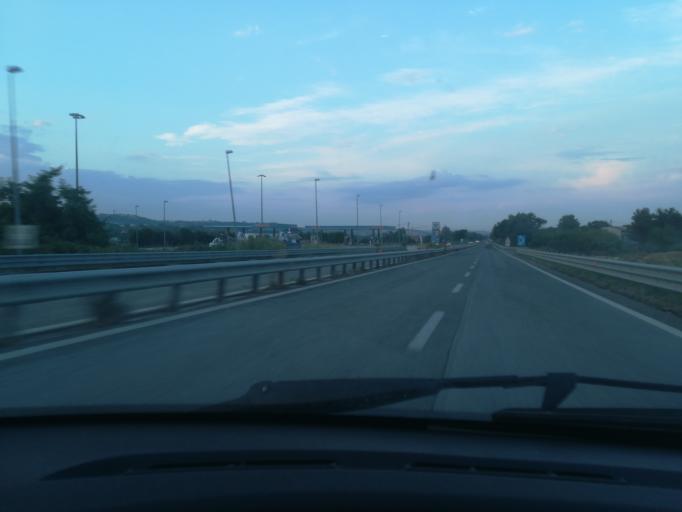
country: IT
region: The Marches
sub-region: Provincia di Macerata
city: Sforzacosta
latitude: 43.2500
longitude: 13.4371
